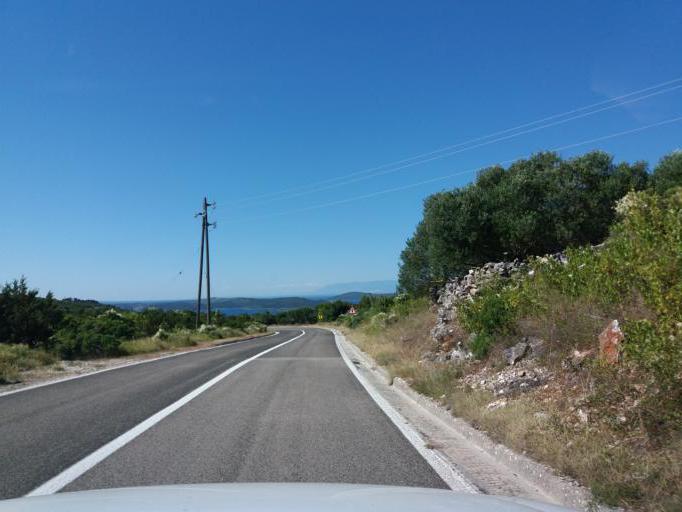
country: HR
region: Zadarska
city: Ugljan
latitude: 44.0975
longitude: 14.9438
